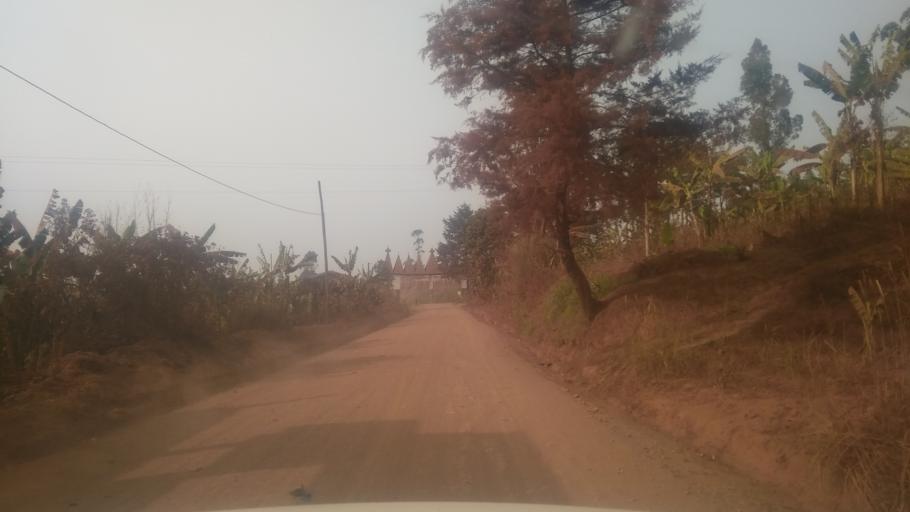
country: CM
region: West
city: Dschang
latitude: 5.4835
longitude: 10.1063
